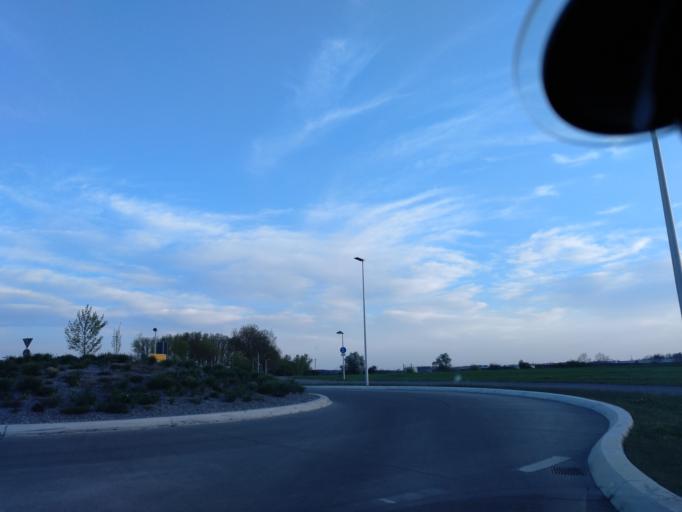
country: DE
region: Baden-Wuerttemberg
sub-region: Regierungsbezirk Stuttgart
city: Crailsheim
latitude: 49.1346
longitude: 10.0352
